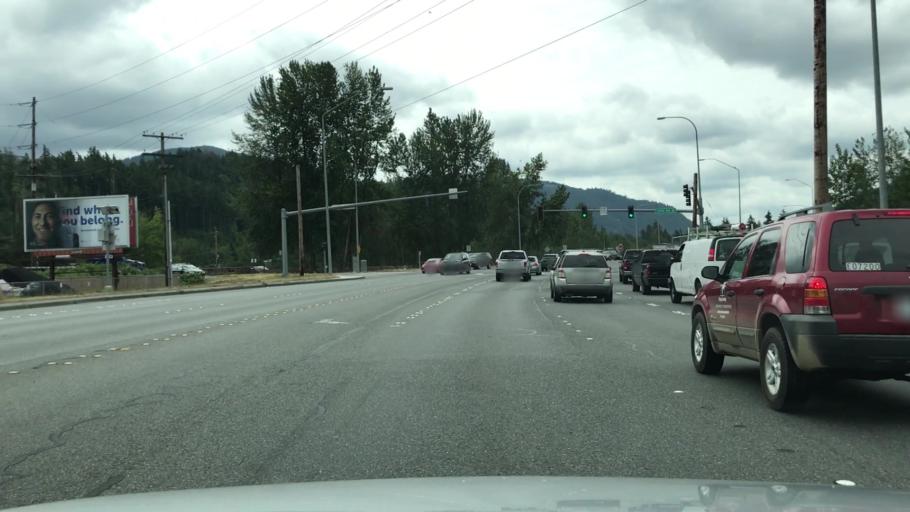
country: US
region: Washington
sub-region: King County
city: Issaquah
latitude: 47.5436
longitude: -122.0363
